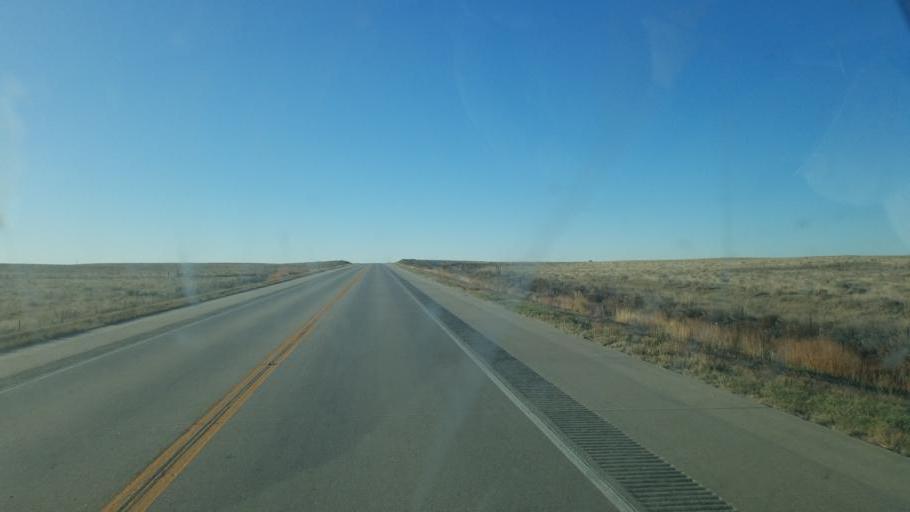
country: US
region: Colorado
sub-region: Kiowa County
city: Eads
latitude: 38.5431
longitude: -102.7860
